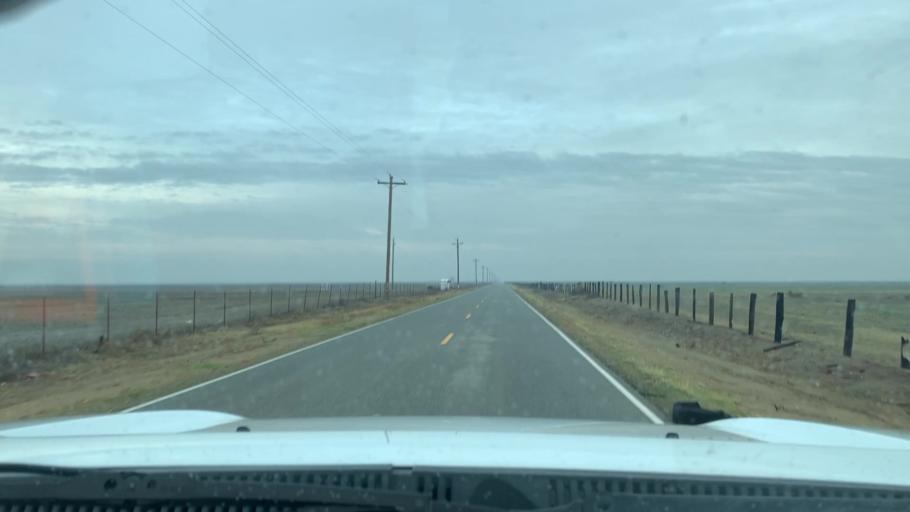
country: US
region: California
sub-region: Kern County
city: Lost Hills
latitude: 35.6814
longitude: -119.5798
